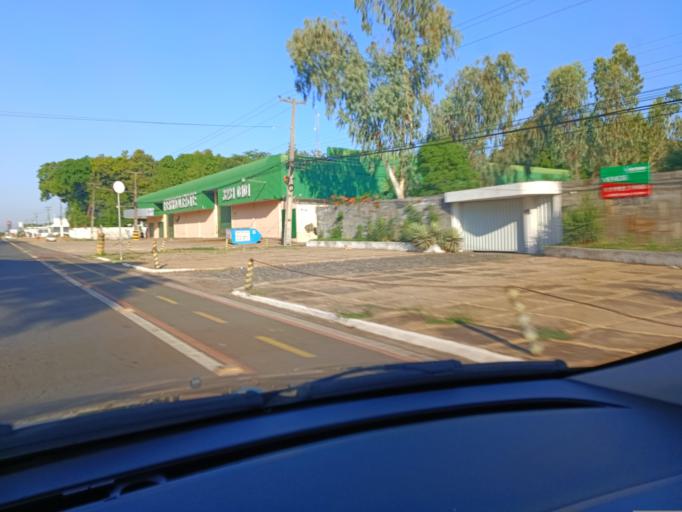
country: BR
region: Piaui
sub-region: Teresina
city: Teresina
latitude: -5.0811
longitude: -42.7631
